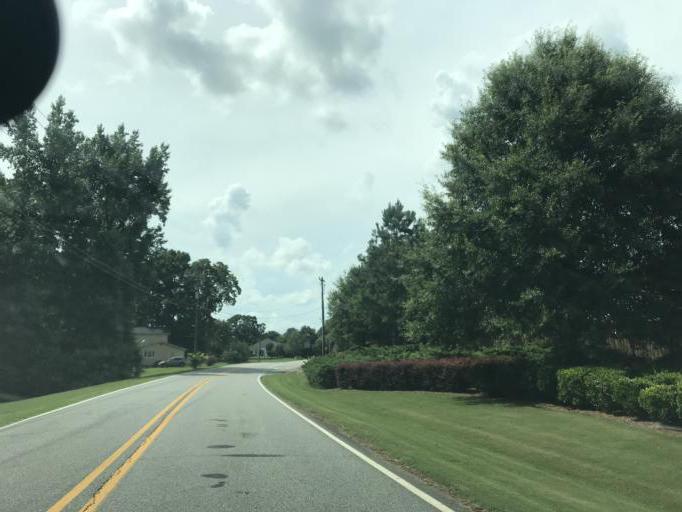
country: US
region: Georgia
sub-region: Forsyth County
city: Cumming
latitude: 34.2325
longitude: -84.2437
